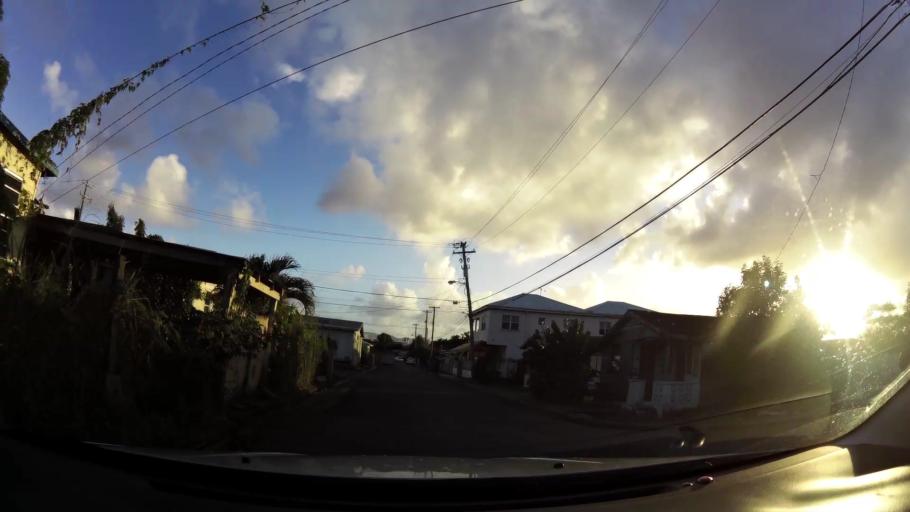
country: AG
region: Saint John
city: Saint John's
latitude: 17.1326
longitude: -61.8475
